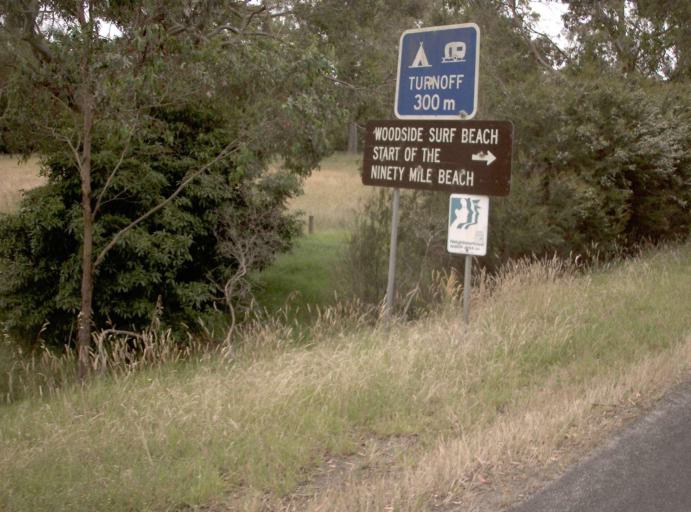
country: AU
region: Victoria
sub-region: Wellington
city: Sale
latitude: -38.5259
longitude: 146.8714
